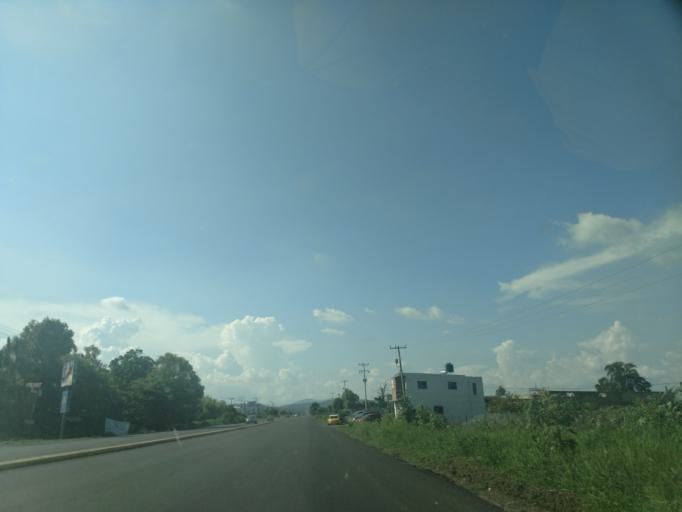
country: MX
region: Jalisco
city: Ahualulco de Mercado
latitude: 20.7111
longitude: -103.9747
